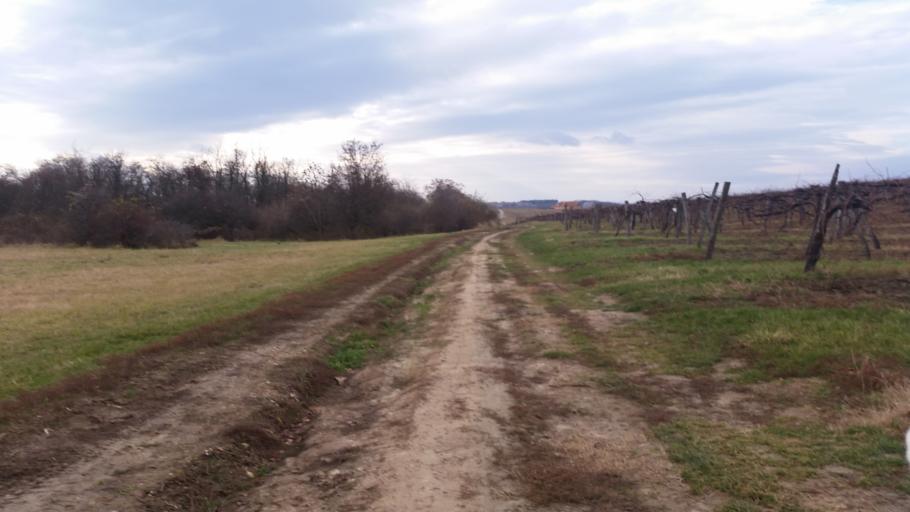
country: HU
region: Pest
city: Telki
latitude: 47.5686
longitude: 18.8127
